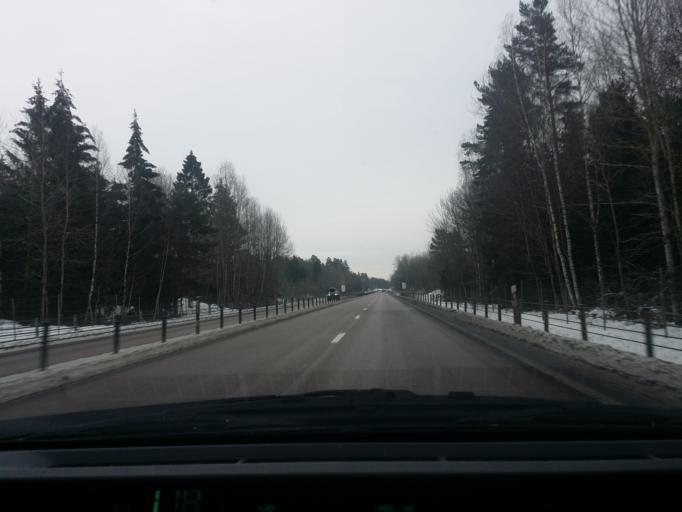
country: SE
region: Vaestra Goetaland
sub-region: Skovde Kommun
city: Stopen
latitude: 58.5216
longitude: 13.8266
